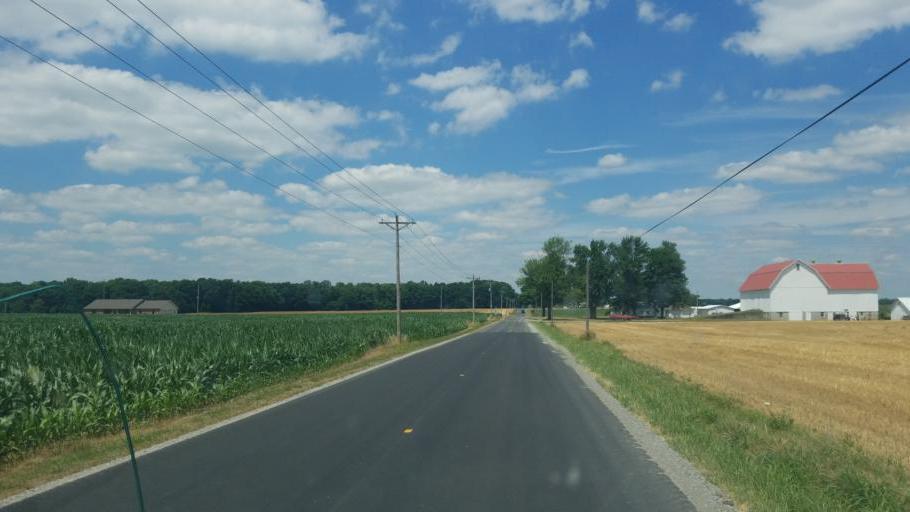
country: US
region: Ohio
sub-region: Williams County
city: Edgerton
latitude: 41.4390
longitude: -84.7103
